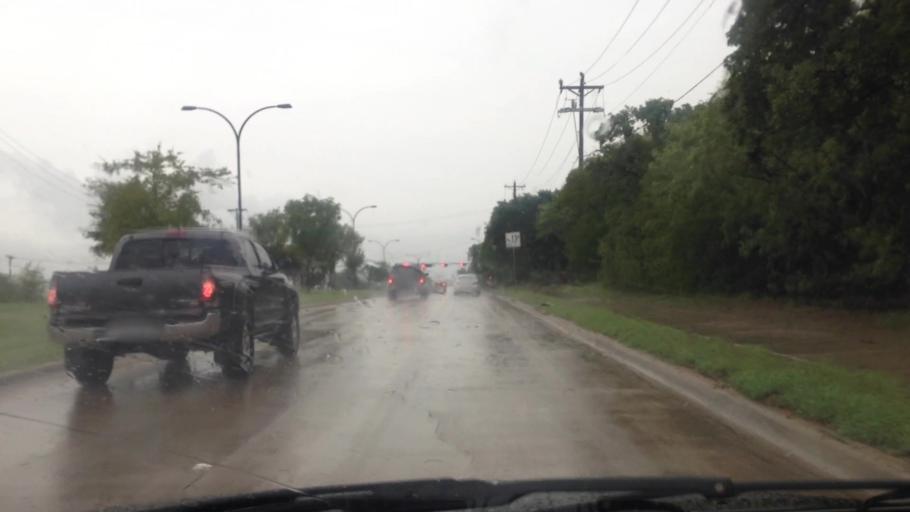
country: US
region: Texas
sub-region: Tarrant County
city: Keller
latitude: 32.9103
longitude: -97.2322
